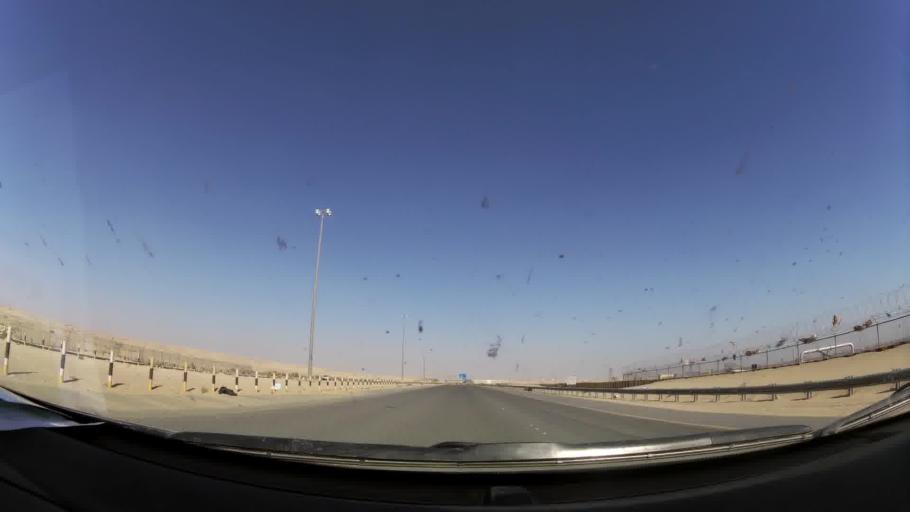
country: KW
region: Muhafazat al Jahra'
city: Al Jahra'
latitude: 29.3992
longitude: 47.6884
